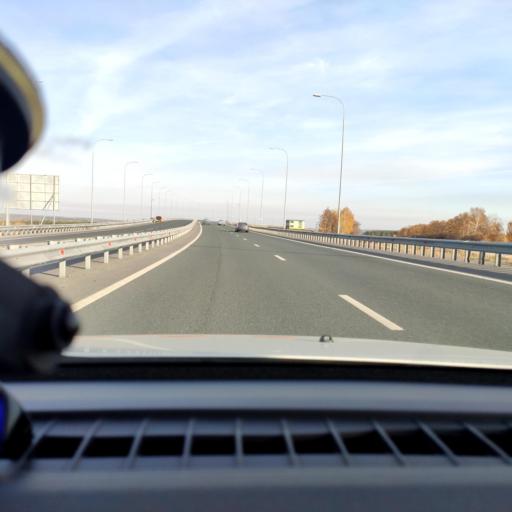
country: RU
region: Samara
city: Bereza
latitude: 53.4955
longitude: 50.1177
